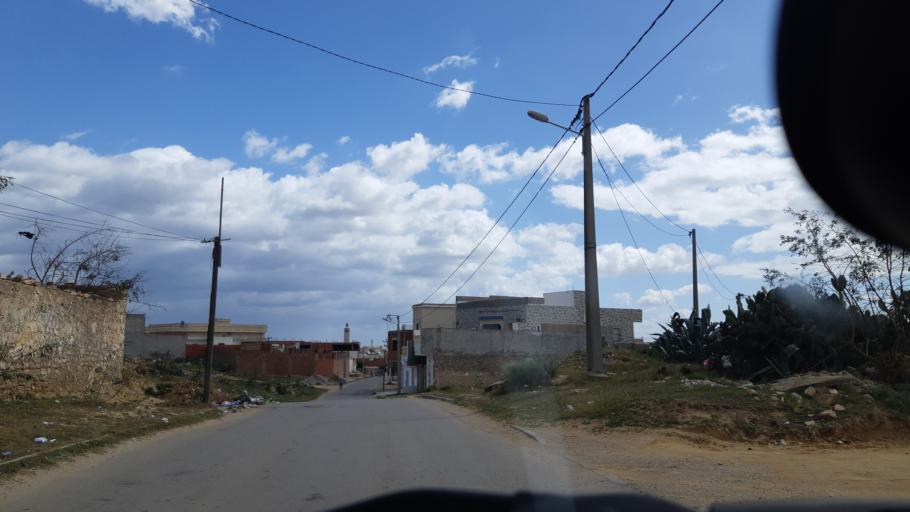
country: TN
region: Susah
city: Akouda
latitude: 35.8768
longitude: 10.5173
